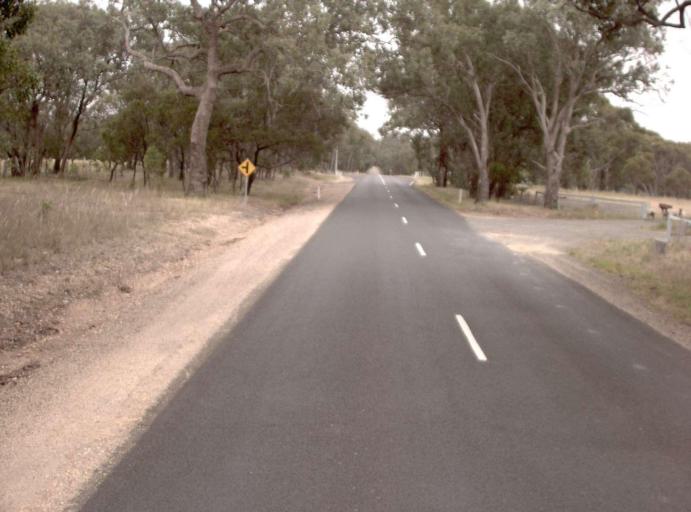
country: AU
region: Victoria
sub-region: Wellington
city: Heyfield
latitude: -37.9651
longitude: 146.7764
